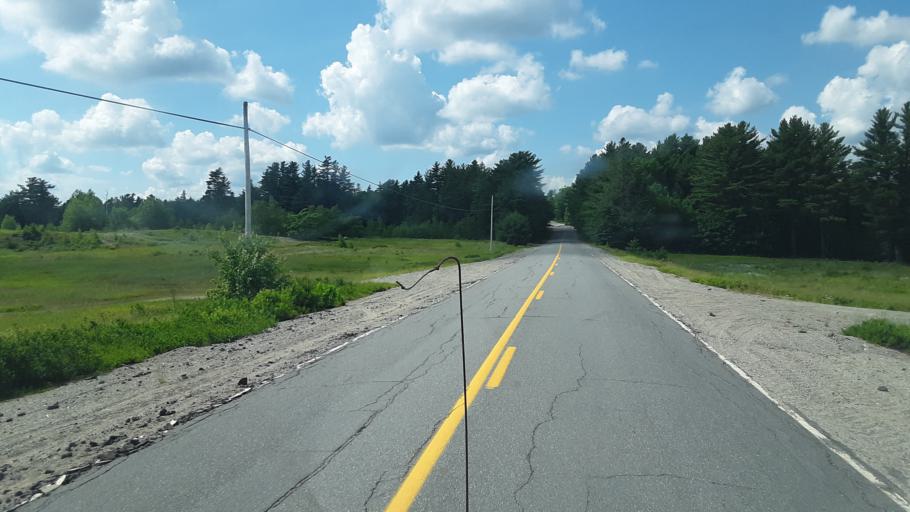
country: US
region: Maine
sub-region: Washington County
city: Machias
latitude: 44.9004
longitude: -67.6290
